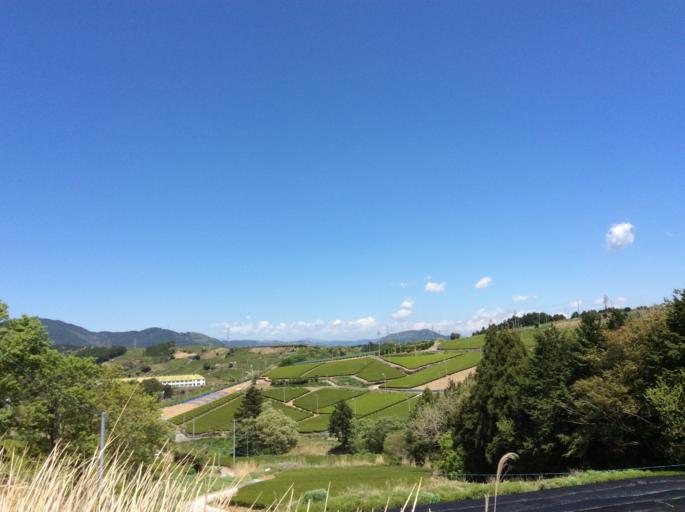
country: JP
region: Shizuoka
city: Kanaya
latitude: 34.8248
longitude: 138.0831
